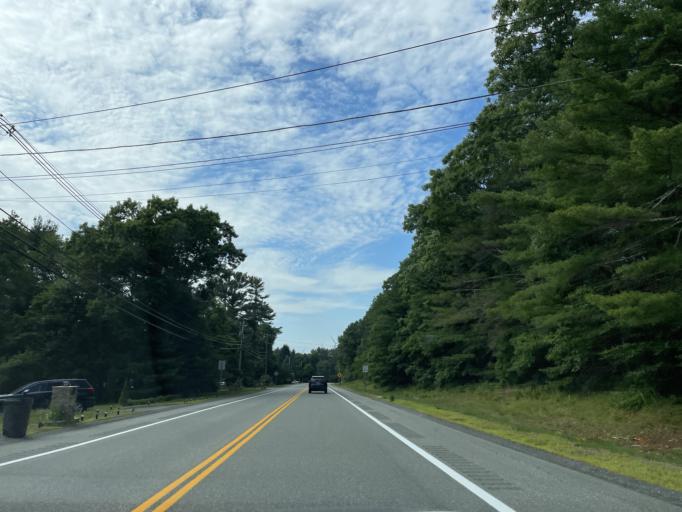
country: US
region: Rhode Island
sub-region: Kent County
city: West Greenwich
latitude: 41.6416
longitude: -71.6899
